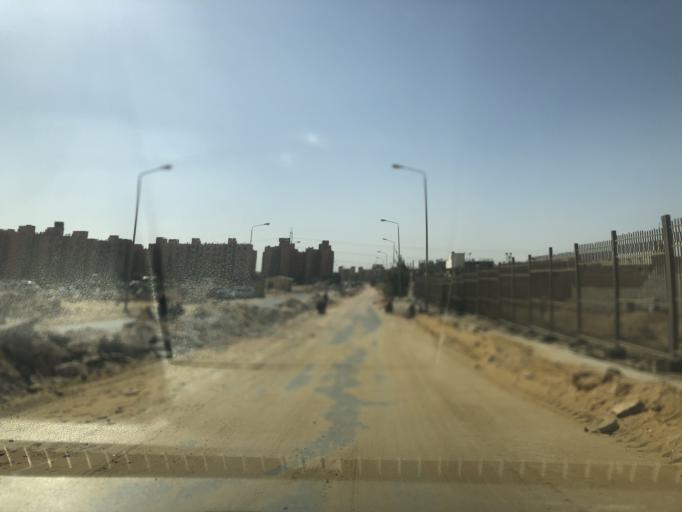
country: EG
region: Al Jizah
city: Madinat Sittah Uktubar
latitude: 29.9281
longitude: 30.9475
